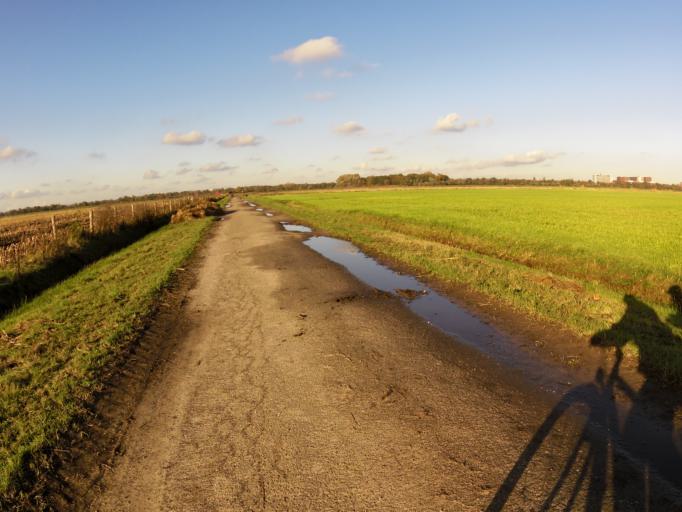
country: NL
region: North Brabant
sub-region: Gemeente Vught
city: Vught
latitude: 51.6727
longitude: 5.2621
